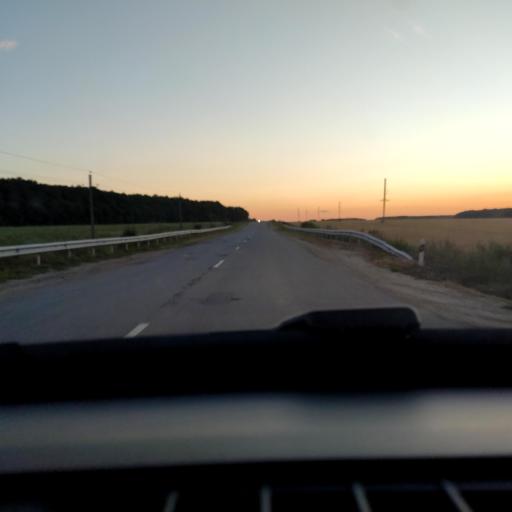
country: RU
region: Lipetsk
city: Zadonsk
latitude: 52.2963
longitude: 38.8360
